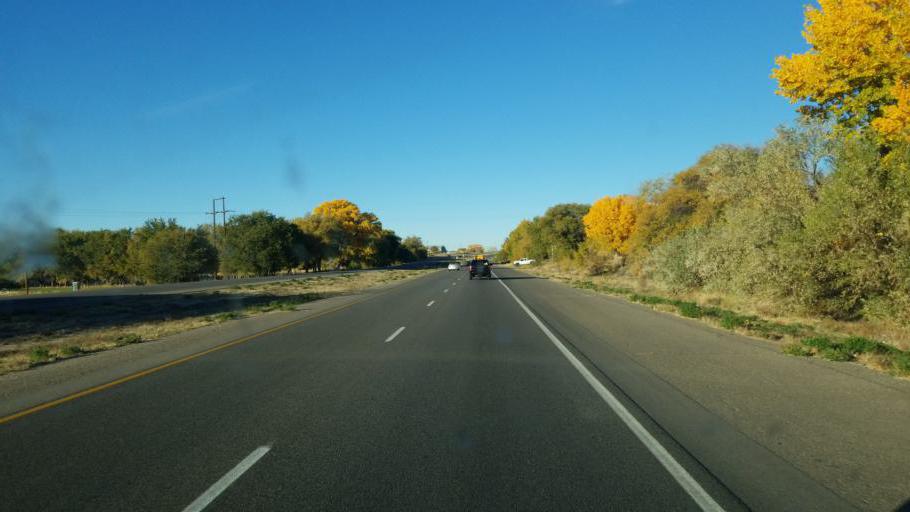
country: US
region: New Mexico
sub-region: San Juan County
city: Shiprock
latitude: 36.7860
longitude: -108.6473
